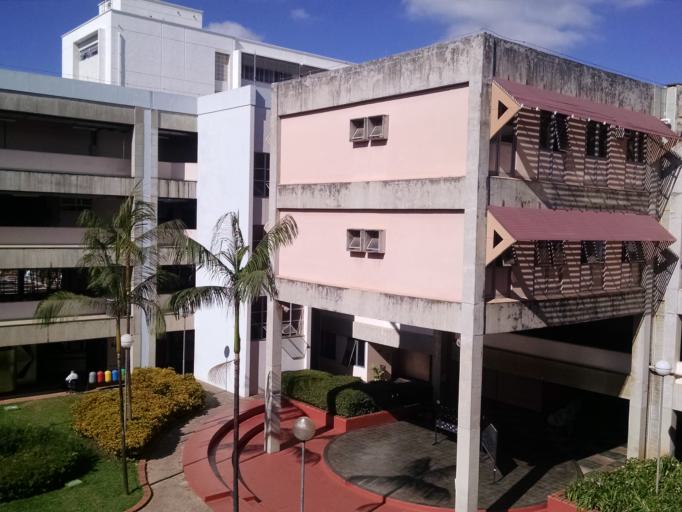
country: BR
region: Minas Gerais
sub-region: Belo Horizonte
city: Belo Horizonte
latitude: -19.8689
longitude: -43.9646
